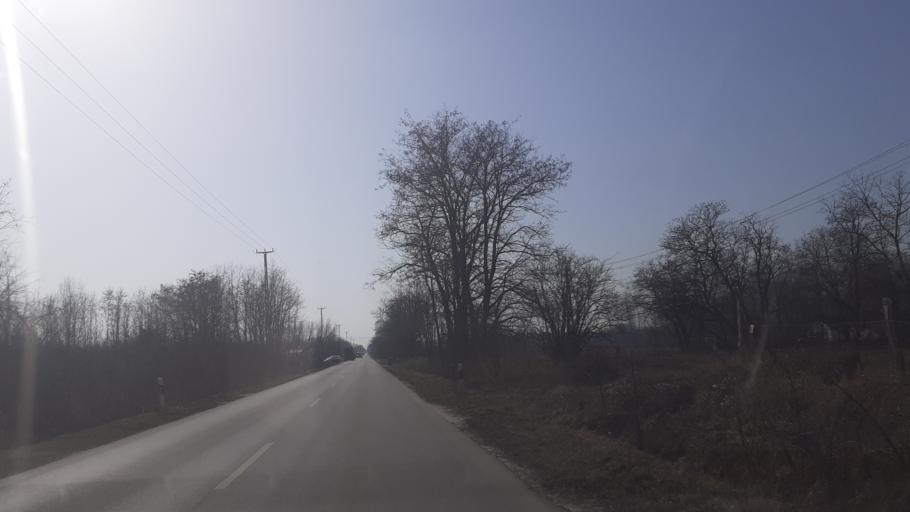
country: HU
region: Bacs-Kiskun
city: Lajosmizse
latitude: 47.0145
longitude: 19.5144
